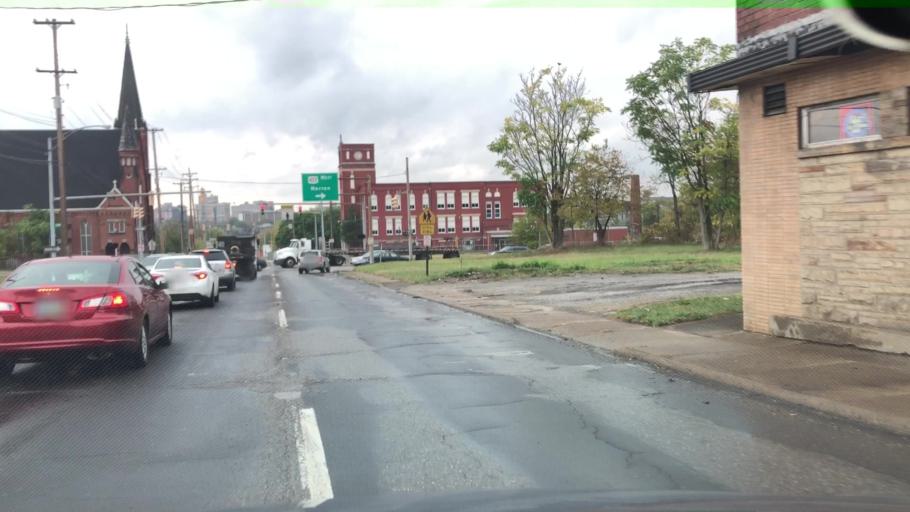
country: US
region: Ohio
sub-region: Mahoning County
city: Youngstown
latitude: 41.1007
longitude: -80.6327
